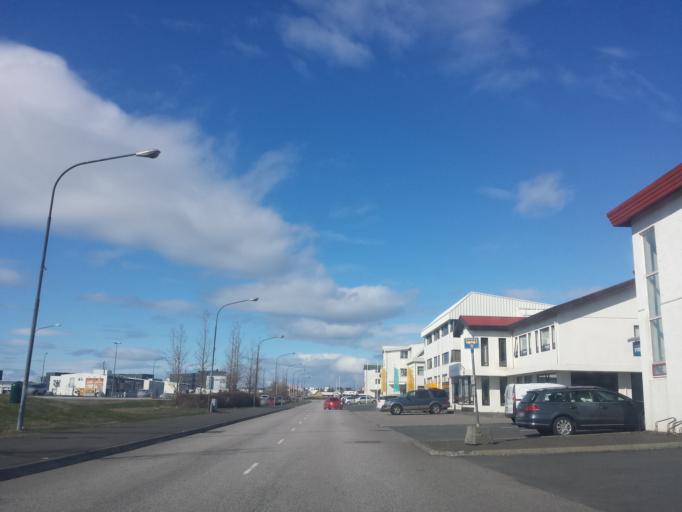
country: IS
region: Capital Region
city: Hafnarfjoerdur
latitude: 64.0790
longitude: -21.9404
